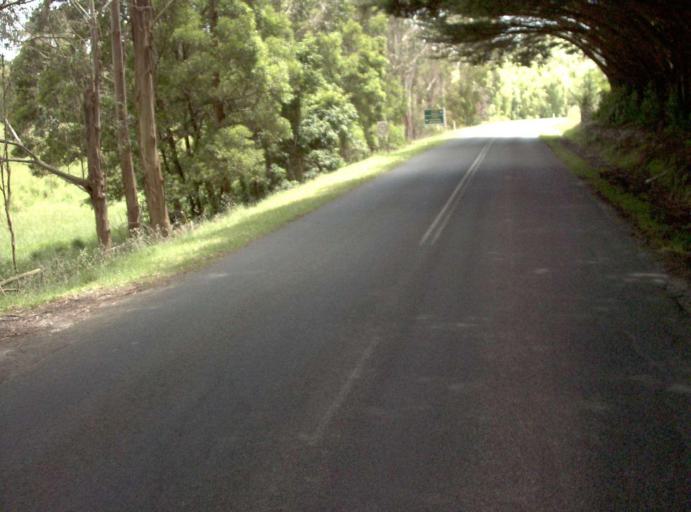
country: AU
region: Victoria
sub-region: Bass Coast
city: North Wonthaggi
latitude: -38.6969
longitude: 146.0872
